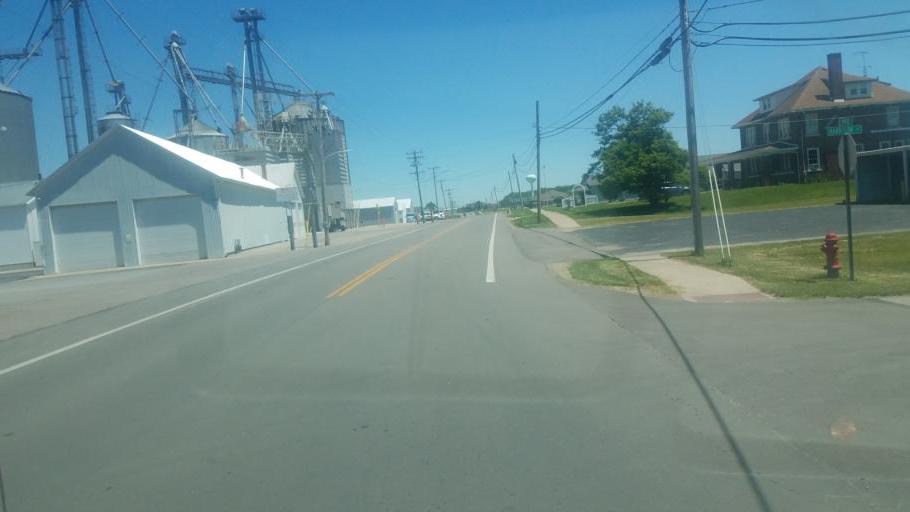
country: US
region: Ohio
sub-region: Darke County
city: Versailles
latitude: 40.2236
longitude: -84.4718
